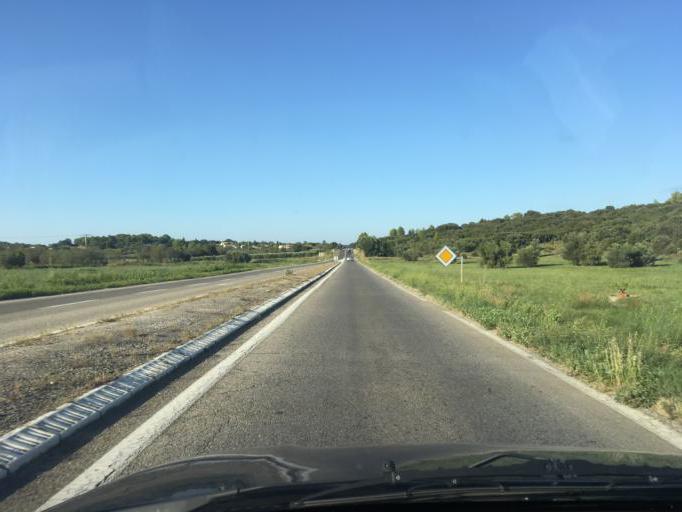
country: FR
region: Languedoc-Roussillon
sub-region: Departement du Gard
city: Ledenon
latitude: 43.9028
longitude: 4.5191
